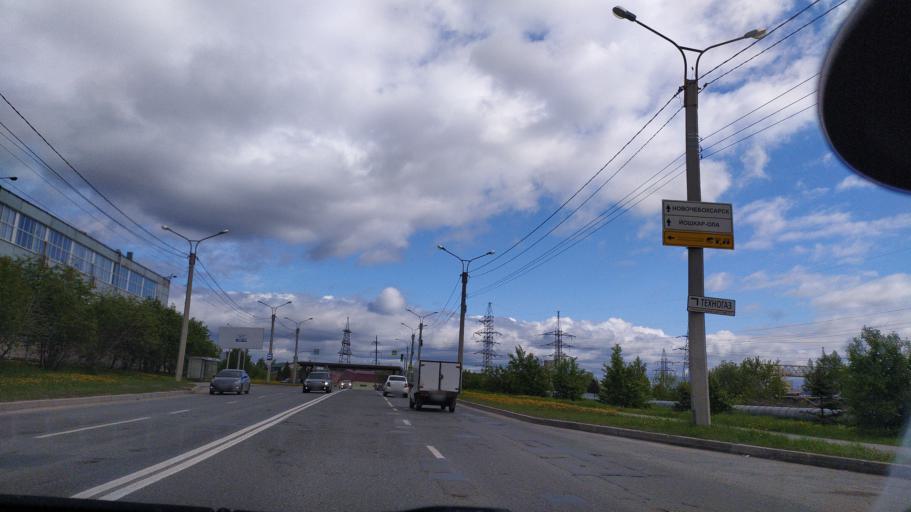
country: RU
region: Chuvashia
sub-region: Cheboksarskiy Rayon
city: Cheboksary
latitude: 56.1157
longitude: 47.2999
